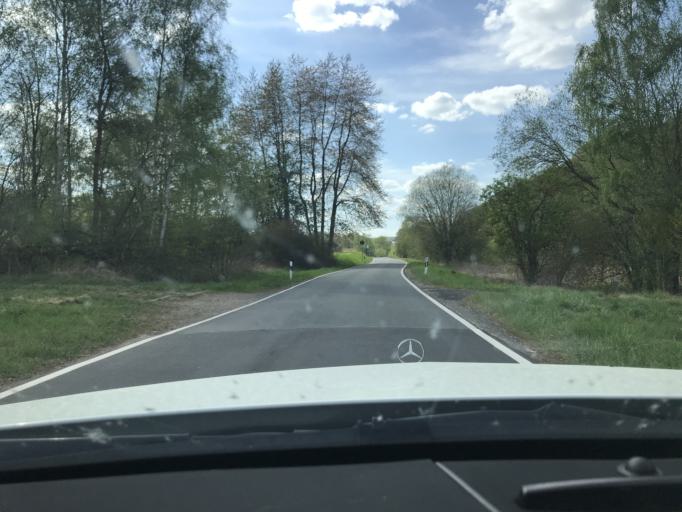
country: DE
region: Hesse
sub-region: Regierungsbezirk Kassel
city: Weissenborn
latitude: 51.1278
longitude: 10.1410
